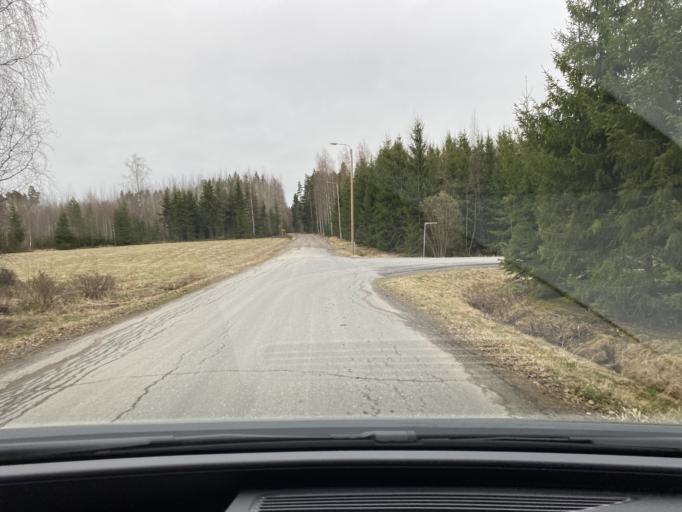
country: FI
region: Satakunta
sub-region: Pori
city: Huittinen
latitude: 61.1606
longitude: 22.7344
